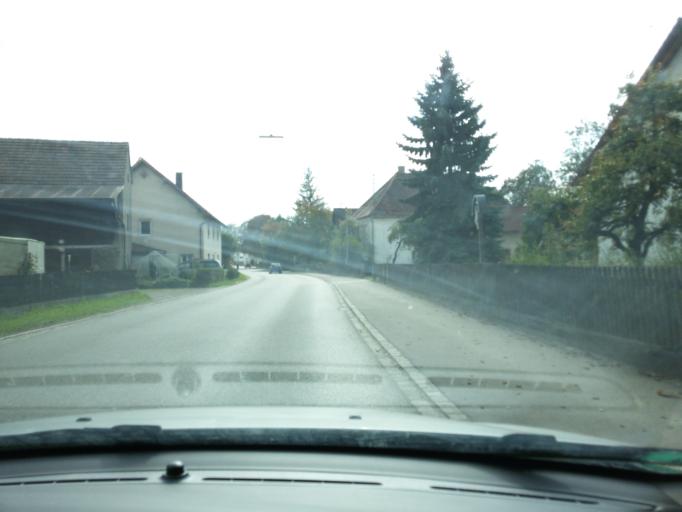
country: DE
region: Bavaria
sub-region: Swabia
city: Lamerdingen
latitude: 48.0923
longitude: 10.7408
